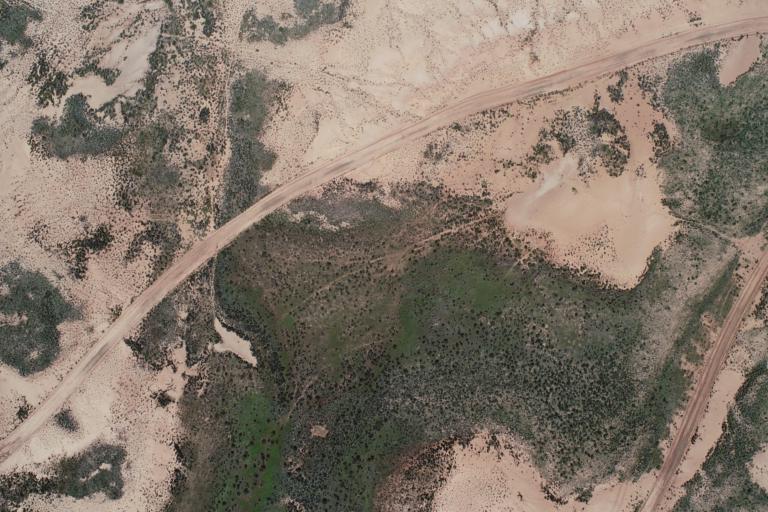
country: BO
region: La Paz
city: Curahuara de Carangas
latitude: -17.2947
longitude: -68.4959
